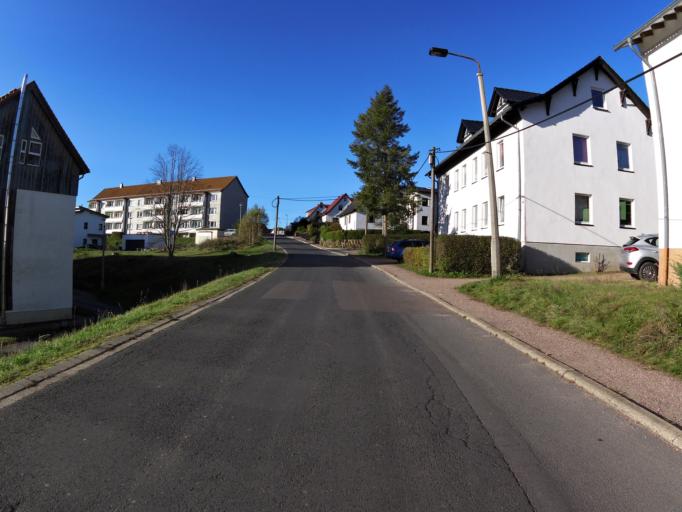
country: DE
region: Thuringia
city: Ruhla
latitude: 50.8826
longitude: 10.3878
